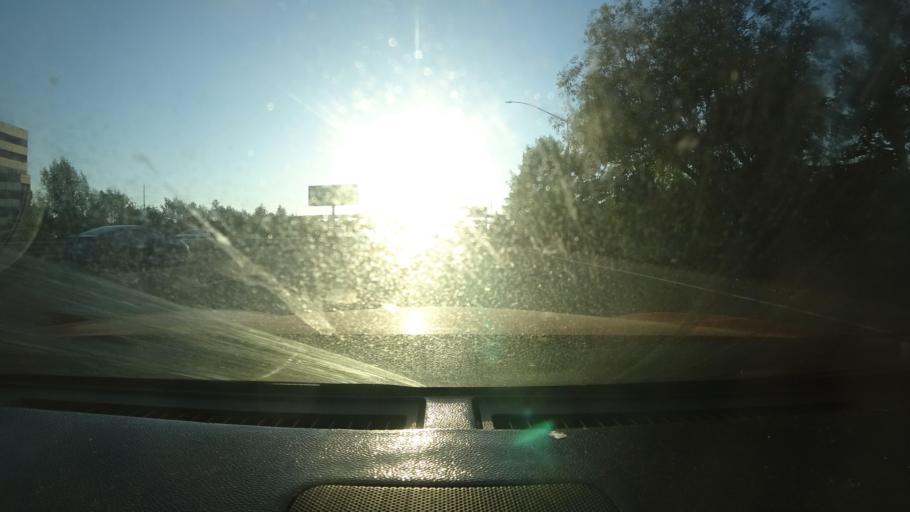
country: US
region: California
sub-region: Santa Clara County
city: Santa Clara
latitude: 37.3731
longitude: -121.9245
